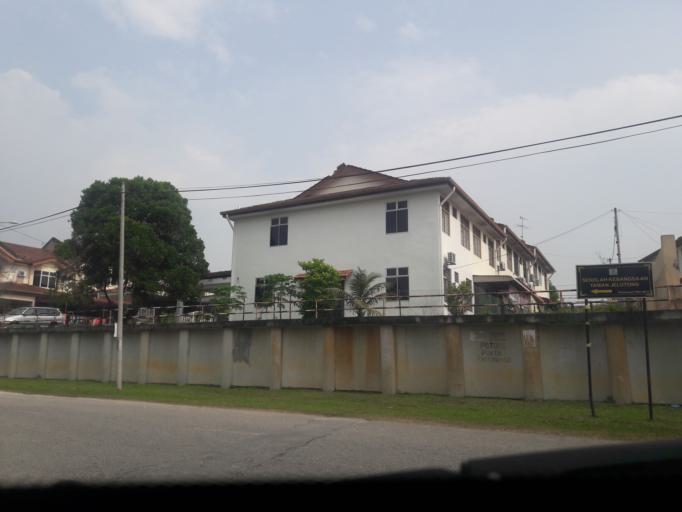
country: MY
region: Kedah
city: Kulim
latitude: 5.3589
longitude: 100.5398
